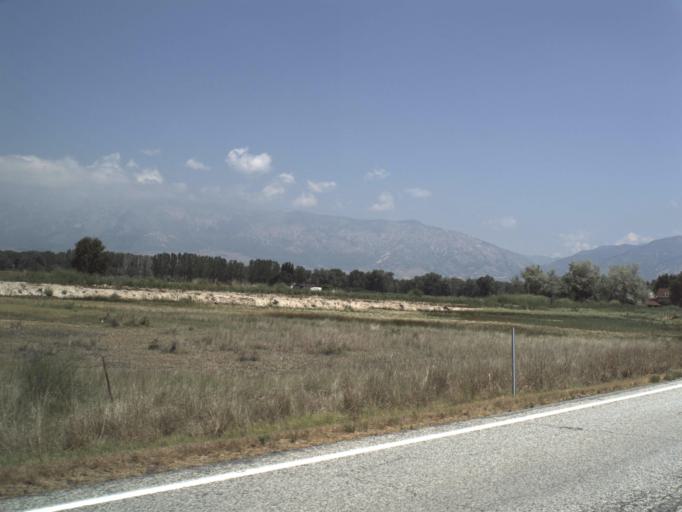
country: US
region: Utah
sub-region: Weber County
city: Marriott-Slaterville
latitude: 41.2443
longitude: -112.0549
